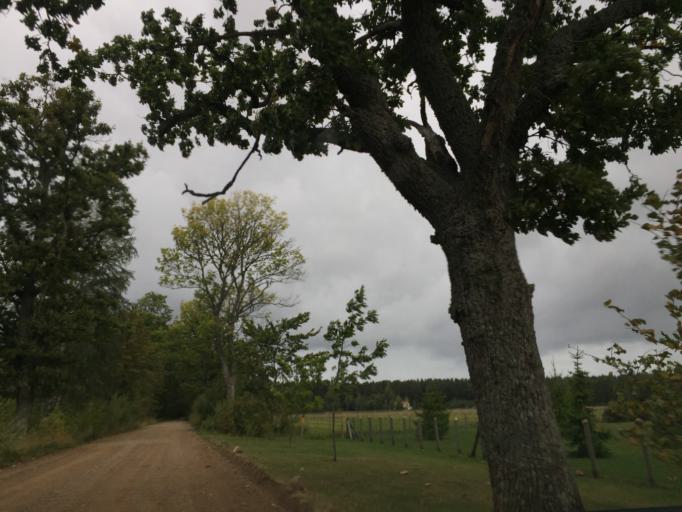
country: LV
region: Salacgrivas
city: Salacgriva
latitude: 57.6738
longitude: 24.3740
